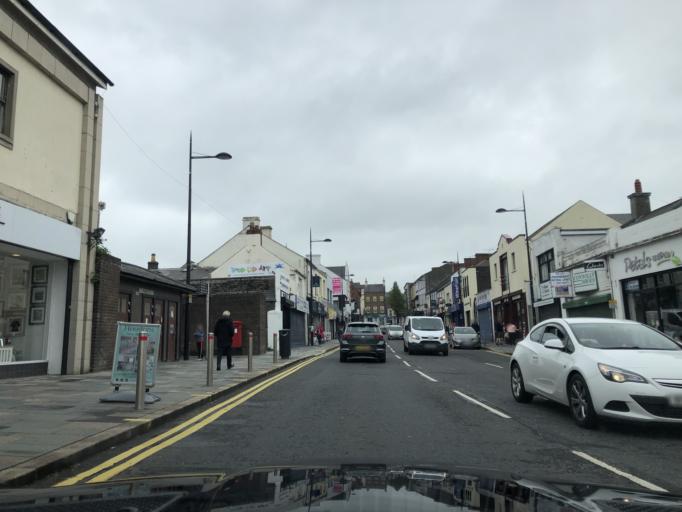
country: GB
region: Northern Ireland
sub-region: Down District
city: Downpatrick
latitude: 54.3276
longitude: -5.7172
